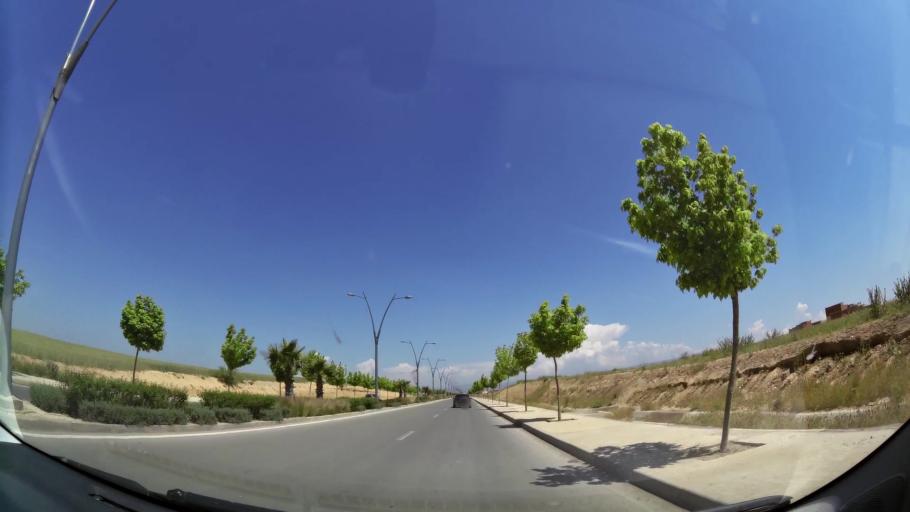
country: MA
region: Oriental
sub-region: Oujda-Angad
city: Oujda
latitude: 34.6966
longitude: -1.9380
